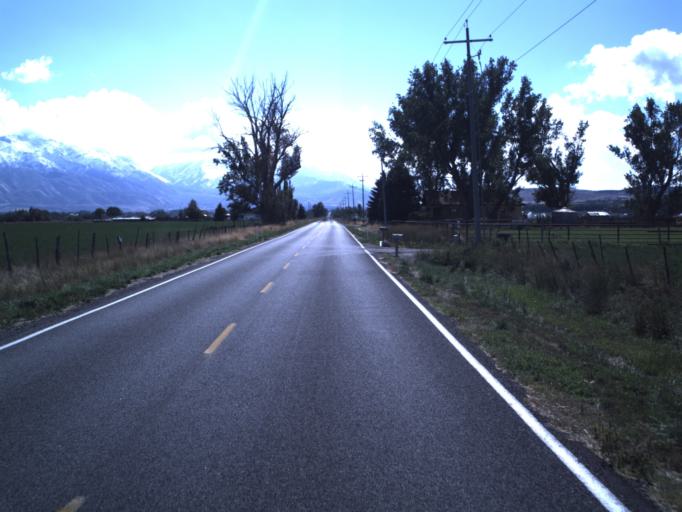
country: US
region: Utah
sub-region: Utah County
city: West Mountain
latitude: 40.0872
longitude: -111.7880
